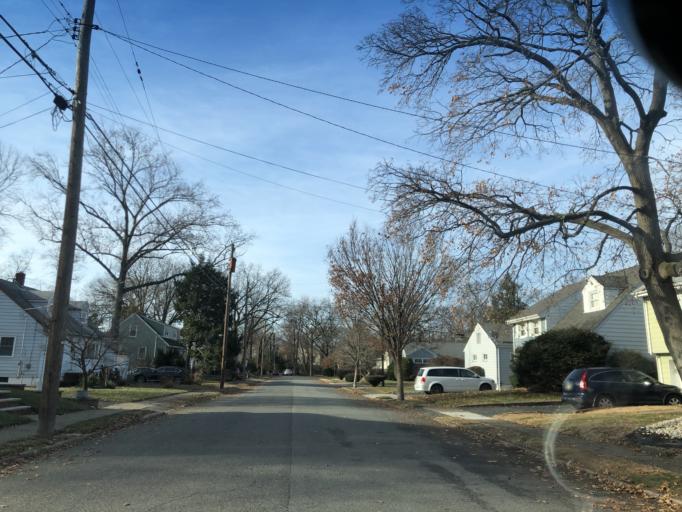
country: US
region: New Jersey
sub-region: Bergen County
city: Fair Lawn
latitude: 40.9261
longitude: -74.1387
